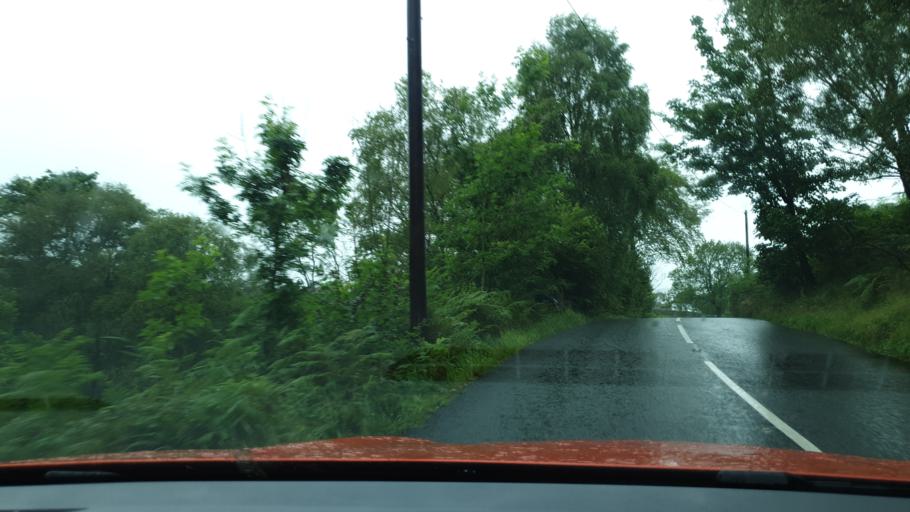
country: GB
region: England
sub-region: Cumbria
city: Ulverston
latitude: 54.3239
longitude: -3.0959
